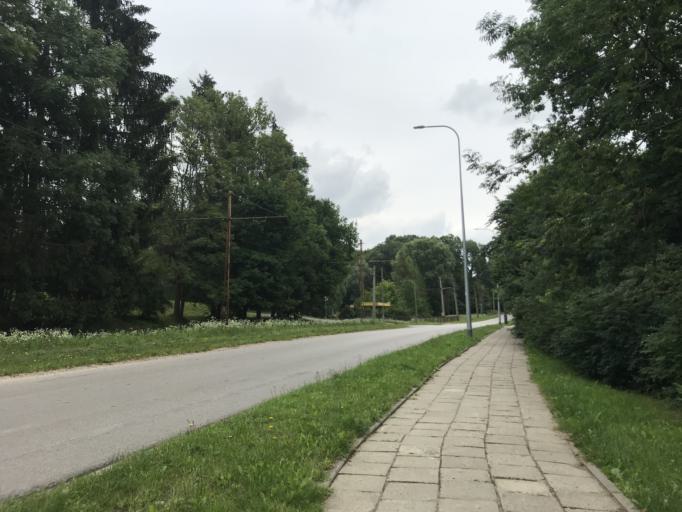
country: PL
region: Warmian-Masurian Voivodeship
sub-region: Powiat elblaski
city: Elblag
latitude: 54.1764
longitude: 19.4336
